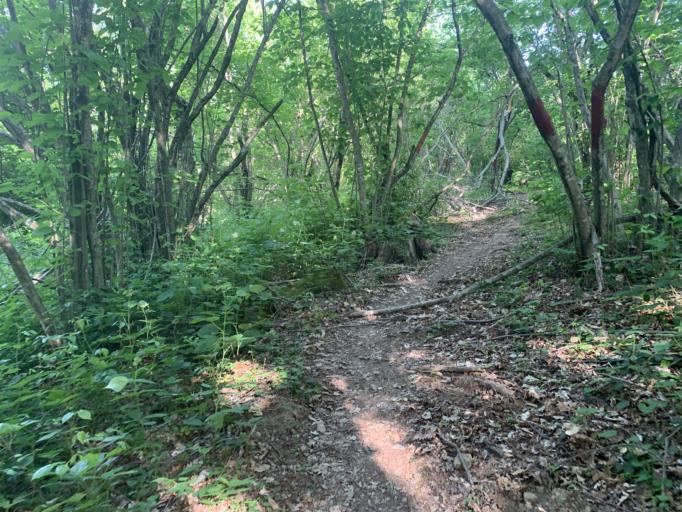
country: RU
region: Krasnodarskiy
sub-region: Sochi City
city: Lazarevskoye
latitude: 43.9513
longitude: 39.3281
